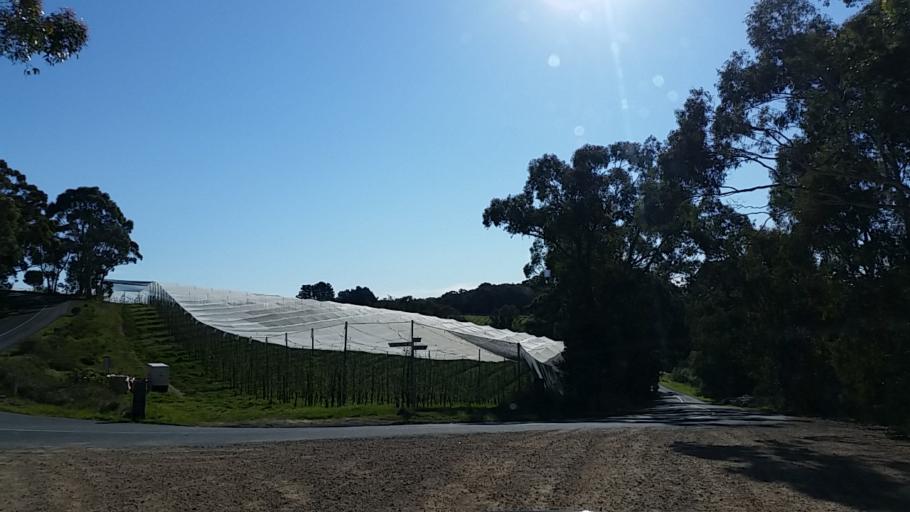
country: AU
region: South Australia
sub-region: Adelaide Hills
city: Lobethal
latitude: -34.8922
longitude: 138.8419
